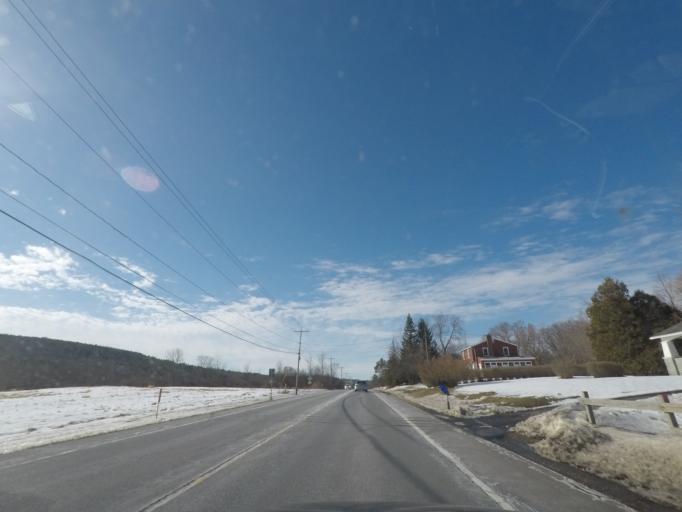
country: US
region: New York
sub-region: Albany County
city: Altamont
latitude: 42.7413
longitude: -74.0198
